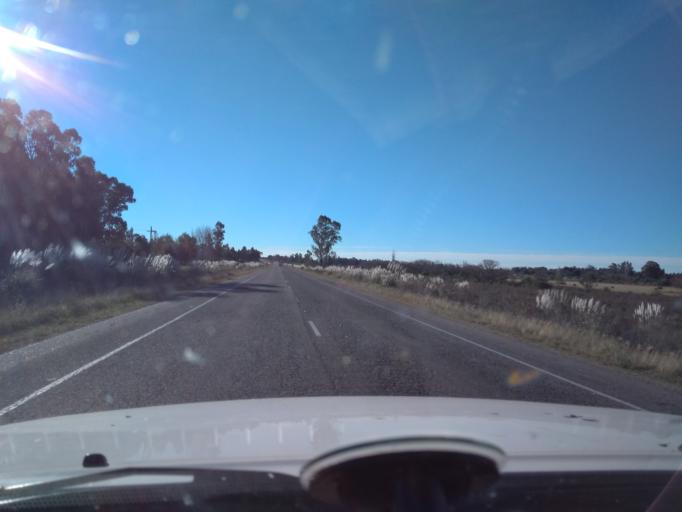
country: UY
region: Canelones
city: Sauce
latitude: -34.6036
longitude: -56.0493
